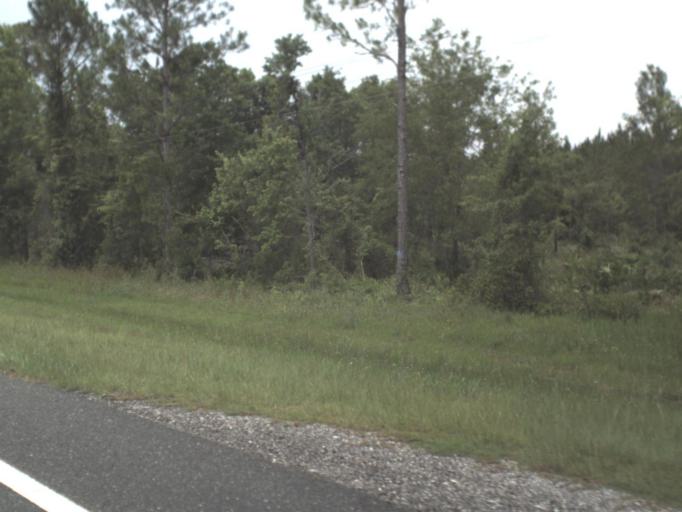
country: US
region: Florida
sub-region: Levy County
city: Chiefland
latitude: 29.3378
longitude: -82.7750
